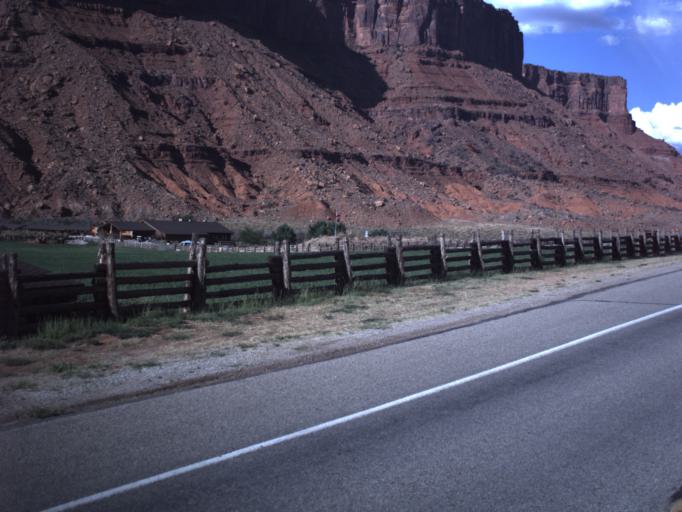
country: US
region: Utah
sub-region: Grand County
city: Moab
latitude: 38.6777
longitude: -109.4484
